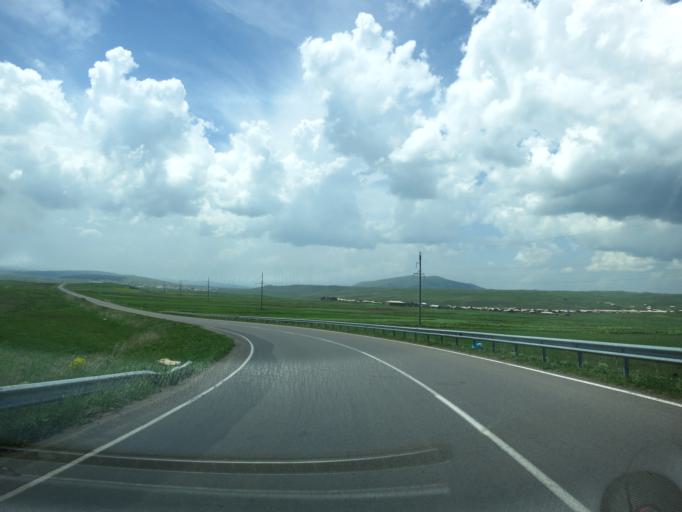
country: GE
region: Samtskhe-Javakheti
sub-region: Ninotsminda
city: Ninotsminda
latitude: 41.2968
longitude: 43.6740
